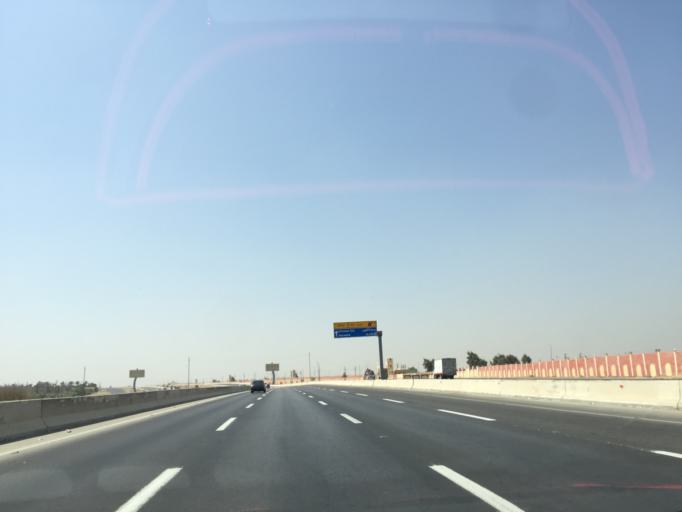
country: EG
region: Al Jizah
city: Awsim
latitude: 30.0818
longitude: 30.9942
